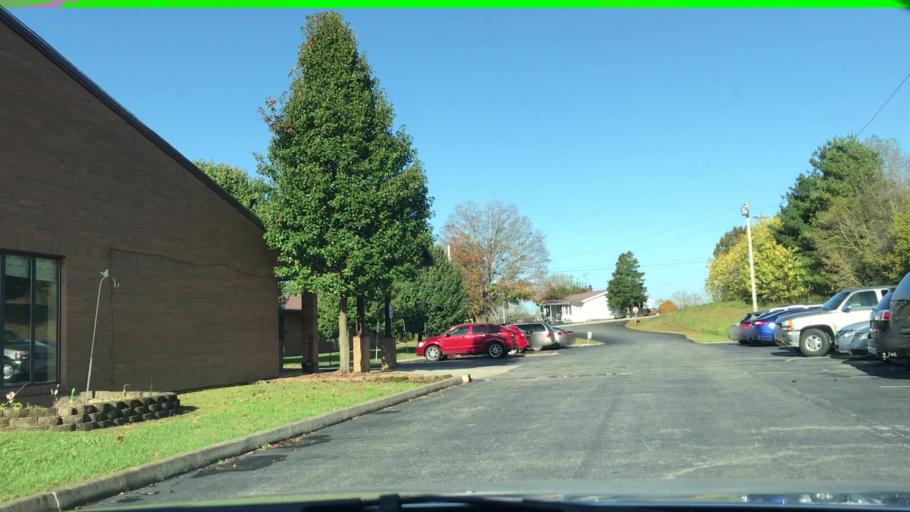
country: US
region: Kentucky
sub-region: Metcalfe County
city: Edmonton
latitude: 36.9885
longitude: -85.6319
